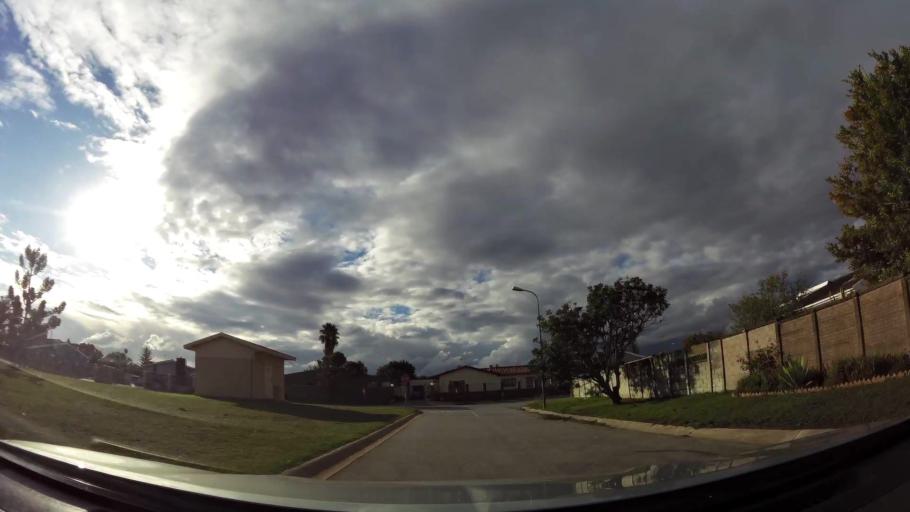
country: ZA
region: Eastern Cape
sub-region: Nelson Mandela Bay Metropolitan Municipality
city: Port Elizabeth
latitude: -33.9469
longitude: 25.4823
